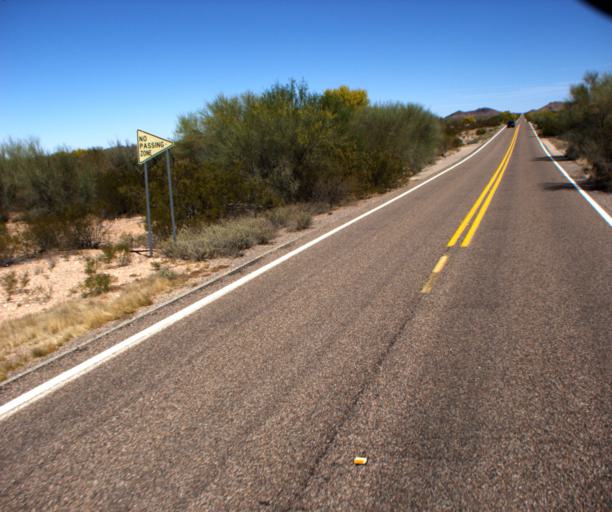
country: MX
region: Sonora
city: Sonoyta
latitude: 32.0441
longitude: -112.7938
